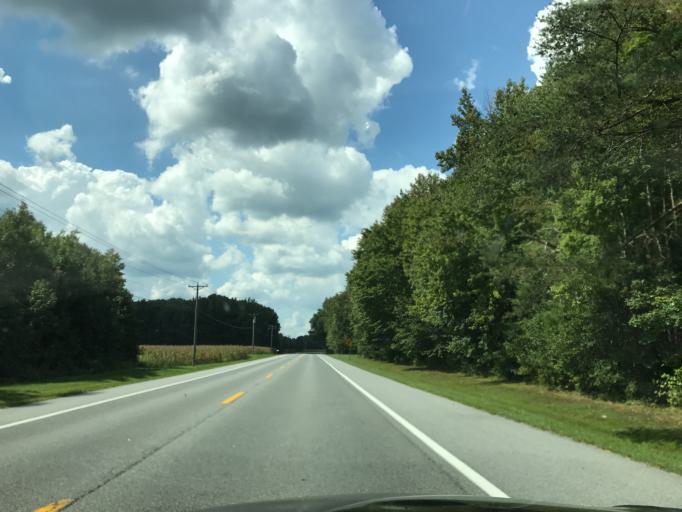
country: US
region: Maryland
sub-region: Caroline County
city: Greensboro
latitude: 39.1445
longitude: -75.8265
